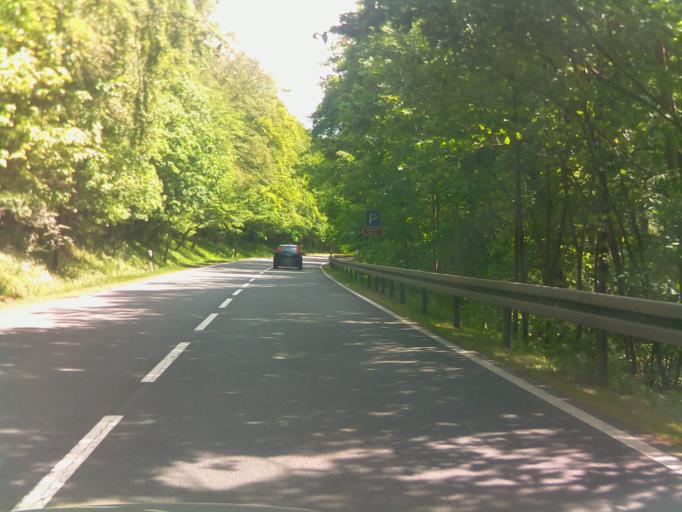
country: DE
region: Saxony-Anhalt
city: Huttenrode
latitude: 51.7241
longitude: 10.8922
